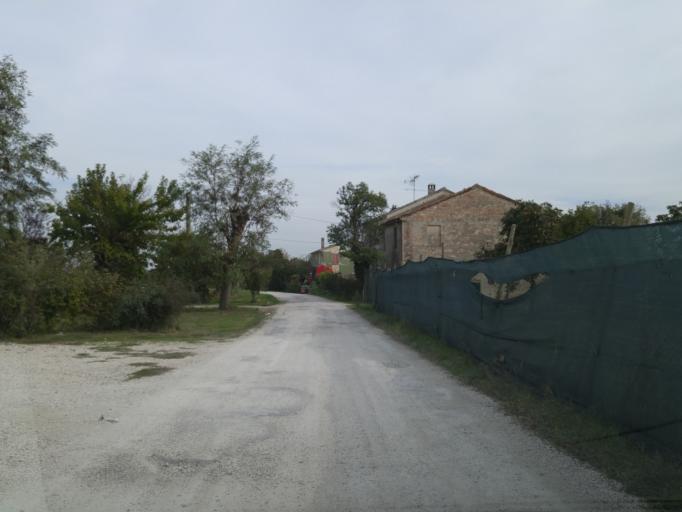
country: IT
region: The Marches
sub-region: Provincia di Pesaro e Urbino
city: Cuccurano
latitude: 43.7707
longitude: 12.9649
